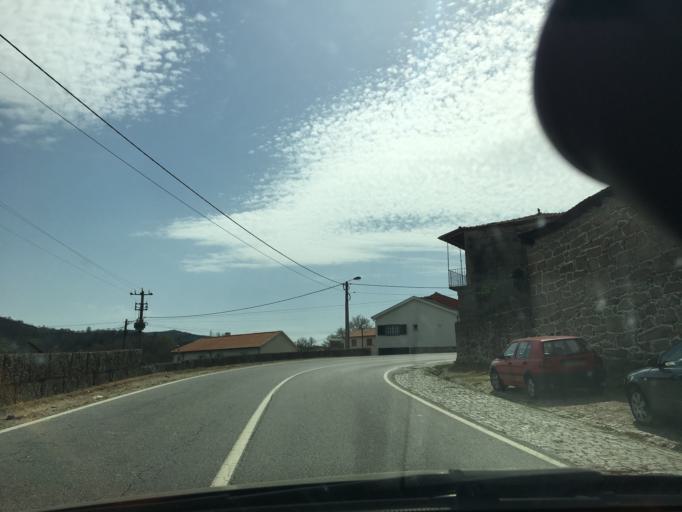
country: PT
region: Vila Real
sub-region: Boticas
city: Boticas
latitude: 41.6846
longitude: -7.6909
